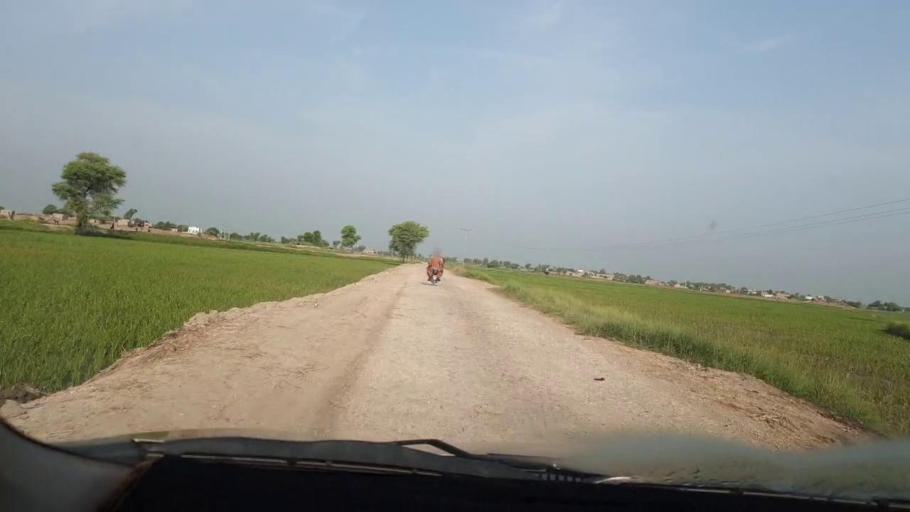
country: PK
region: Sindh
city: Goth Garelo
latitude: 27.4833
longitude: 68.0736
